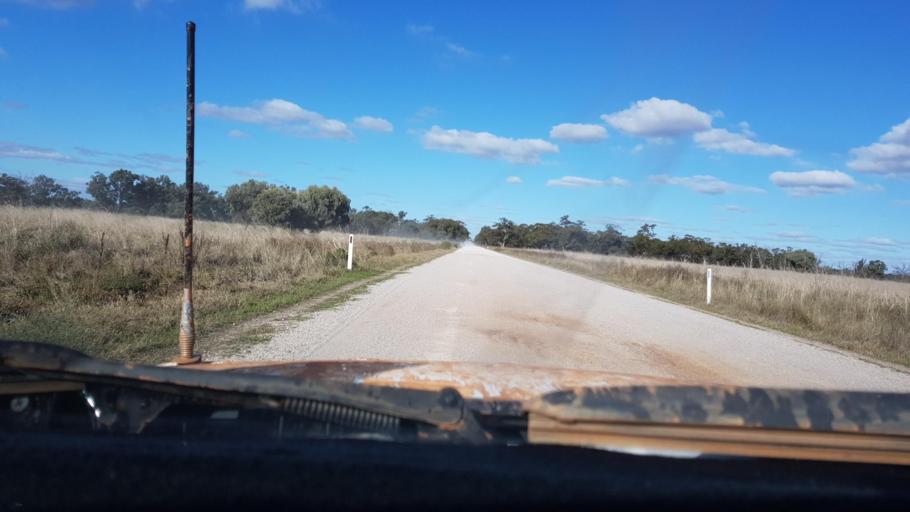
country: AU
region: New South Wales
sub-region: Lachlan
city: Condobolin
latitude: -33.1247
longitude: 147.2488
